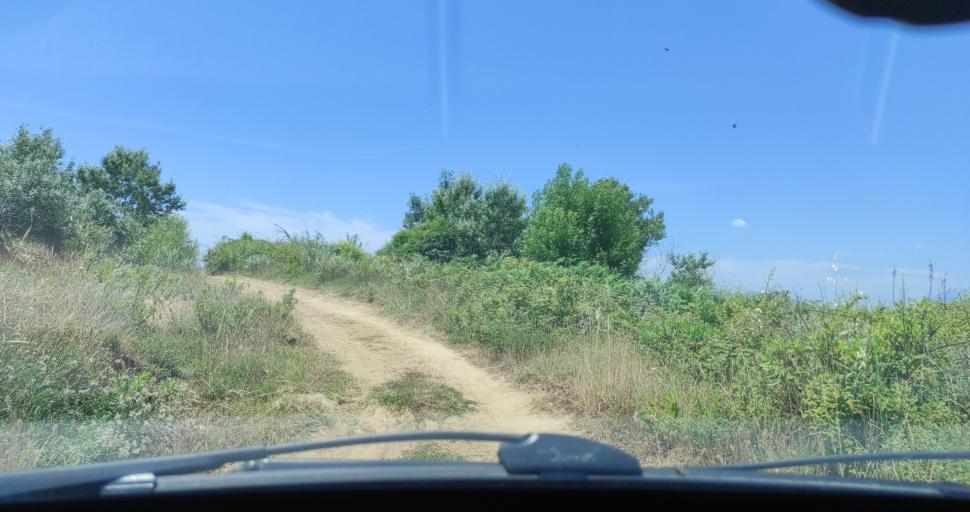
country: AL
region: Shkoder
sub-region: Rrethi i Shkodres
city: Velipoje
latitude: 41.8844
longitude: 19.3882
